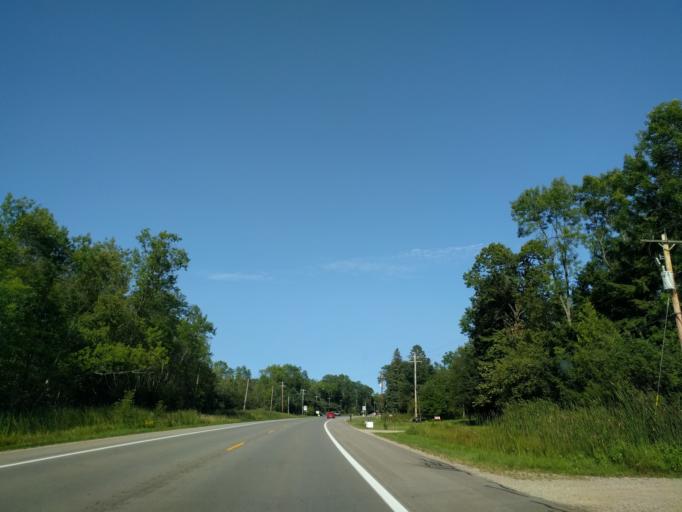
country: US
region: Michigan
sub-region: Menominee County
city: Menominee
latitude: 45.1697
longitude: -87.5831
